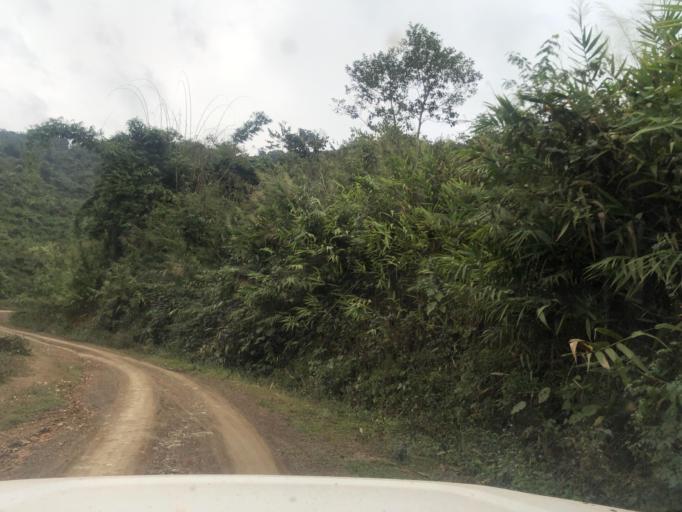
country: LA
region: Phongsali
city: Khoa
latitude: 21.3073
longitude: 102.5830
